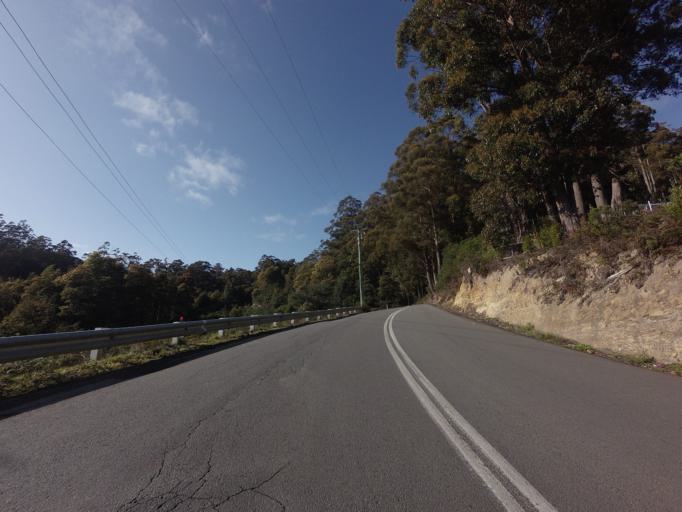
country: AU
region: Tasmania
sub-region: Huon Valley
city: Geeveston
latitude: -43.2493
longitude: 146.9923
